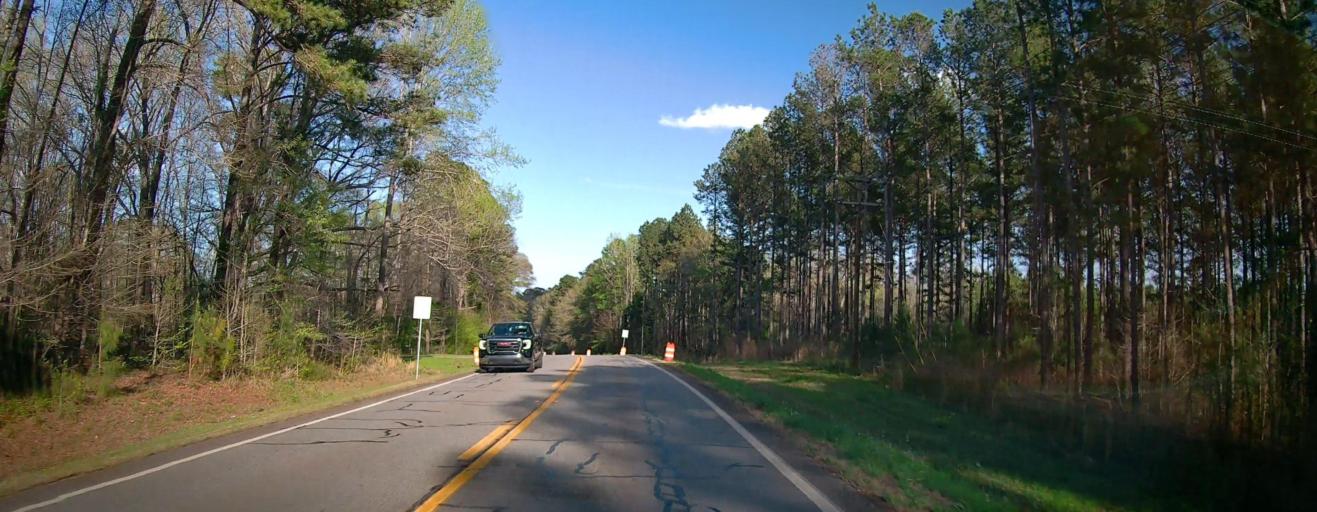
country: US
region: Georgia
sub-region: Baldwin County
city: Milledgeville
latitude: 33.1594
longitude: -83.3620
